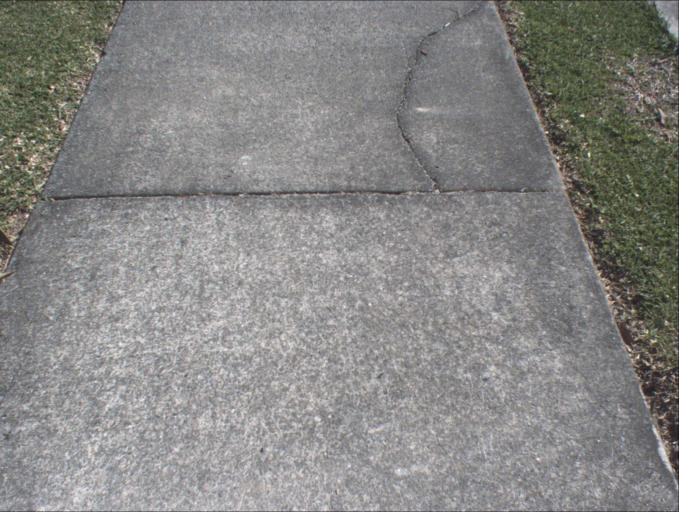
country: AU
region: Queensland
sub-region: Logan
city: Waterford West
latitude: -27.7170
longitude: 153.1433
